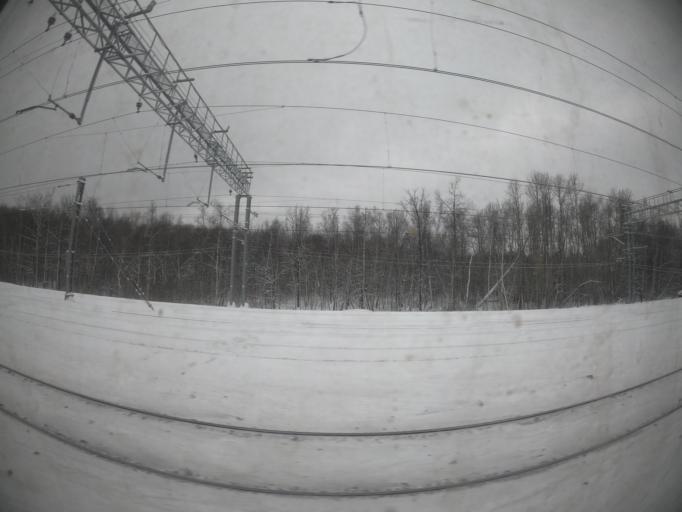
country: RU
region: Moskovskaya
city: Vostryakovo
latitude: 55.4261
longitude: 37.8408
